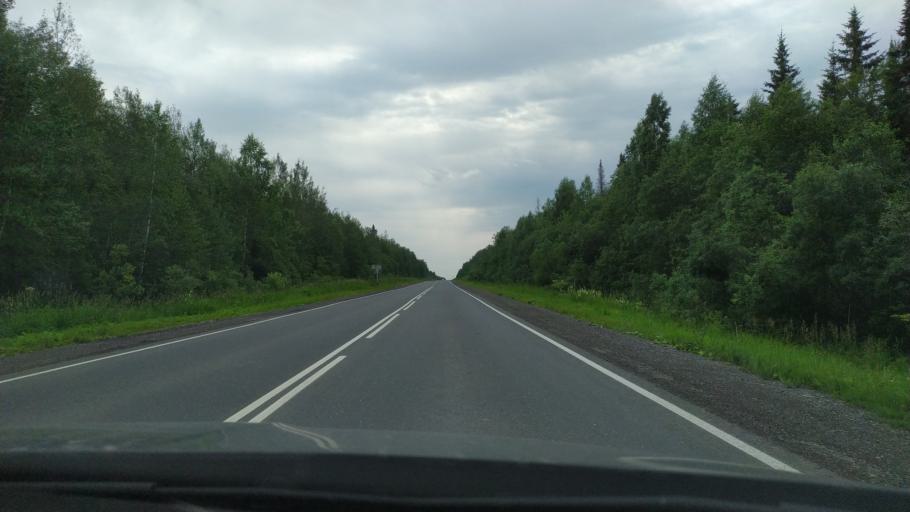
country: RU
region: Perm
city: Chusovoy
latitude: 58.4075
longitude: 57.8749
